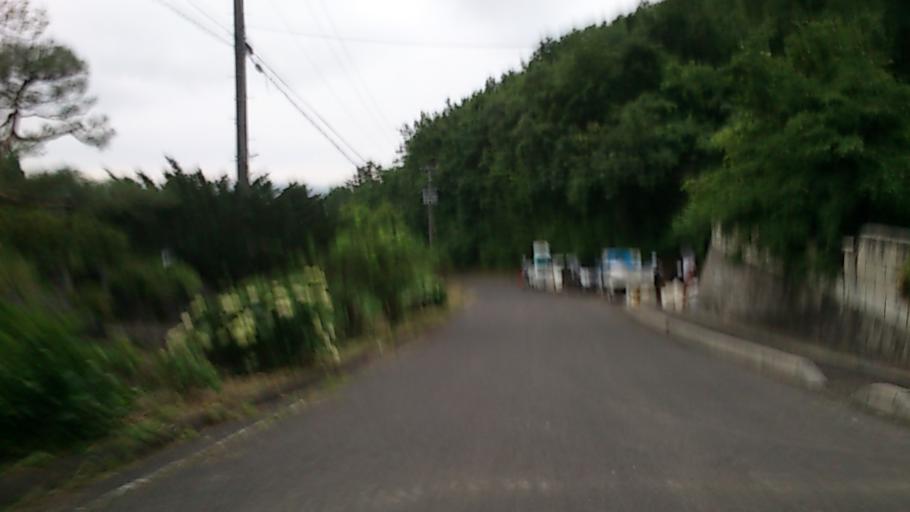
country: JP
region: Fukushima
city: Fukushima-shi
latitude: 37.6887
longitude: 140.5302
